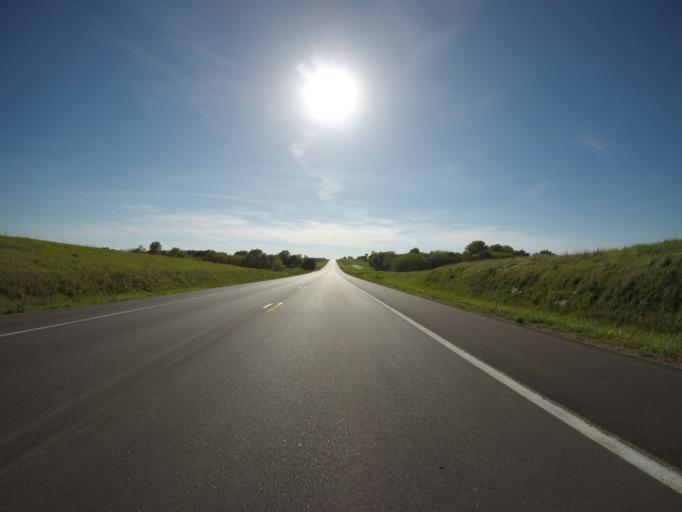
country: US
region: Kansas
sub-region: Clay County
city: Clay Center
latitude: 39.3795
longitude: -96.9862
